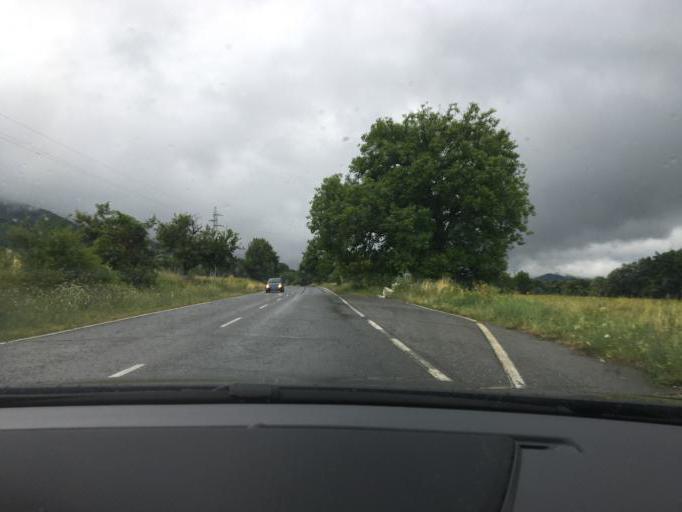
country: BG
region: Kyustendil
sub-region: Obshtina Kyustendil
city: Kyustendil
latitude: 42.2417
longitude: 22.5135
